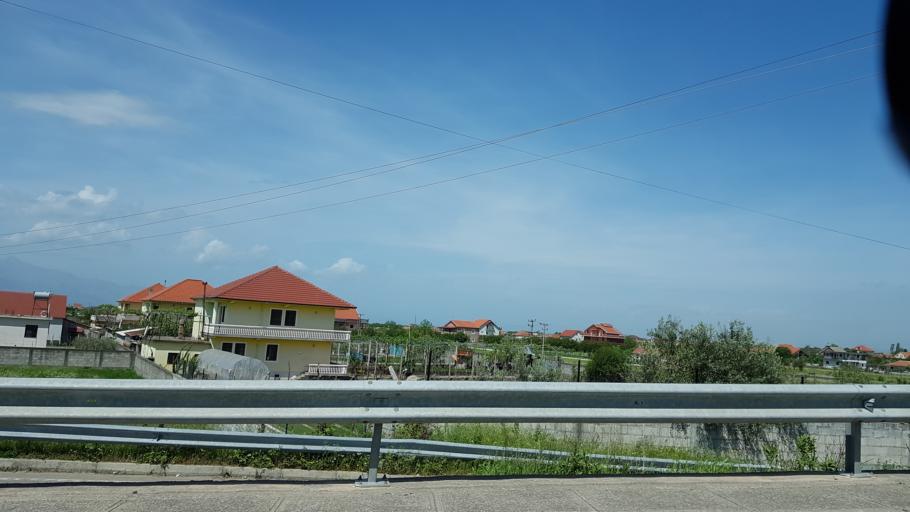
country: AL
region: Shkoder
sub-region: Rrethi i Shkodres
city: Shkoder
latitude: 42.0919
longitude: 19.5346
